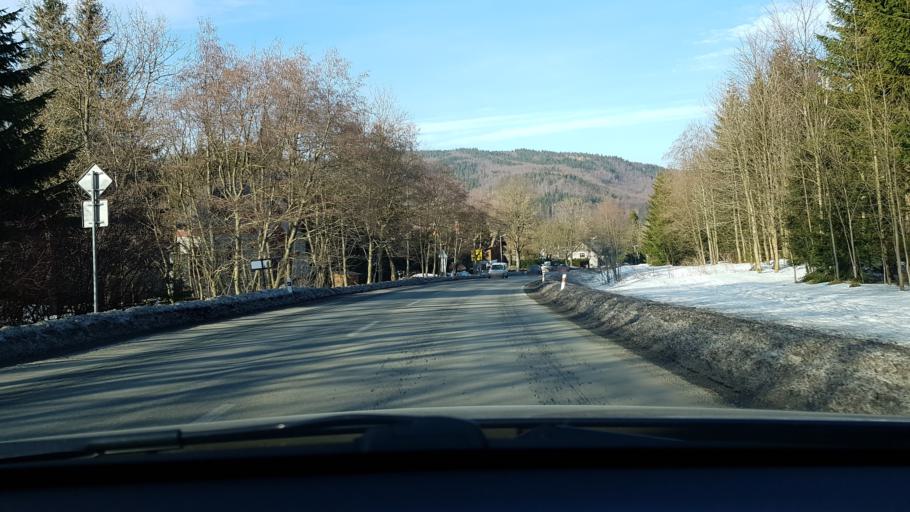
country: CZ
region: Olomoucky
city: Vapenna
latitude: 50.1952
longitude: 17.0647
